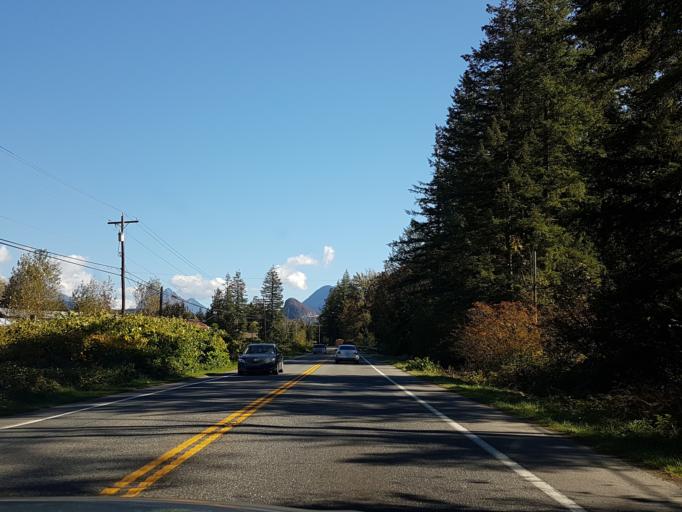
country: US
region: Washington
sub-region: Snohomish County
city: Gold Bar
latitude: 47.8458
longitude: -121.6798
